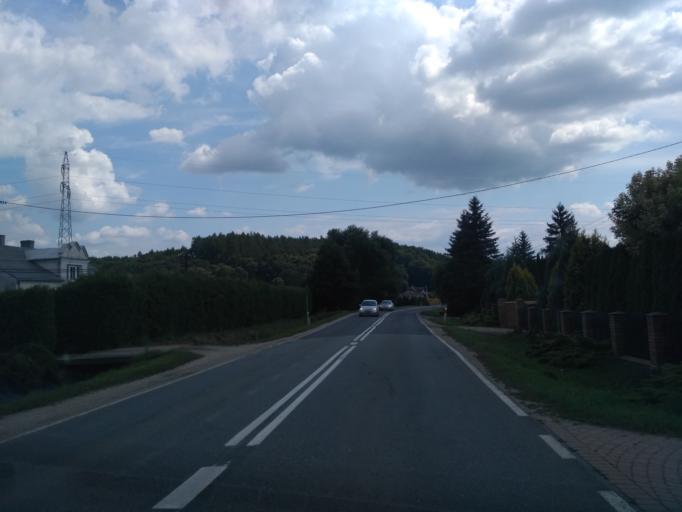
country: PL
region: Subcarpathian Voivodeship
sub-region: Powiat strzyzowski
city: Czudec
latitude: 49.9383
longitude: 21.8151
